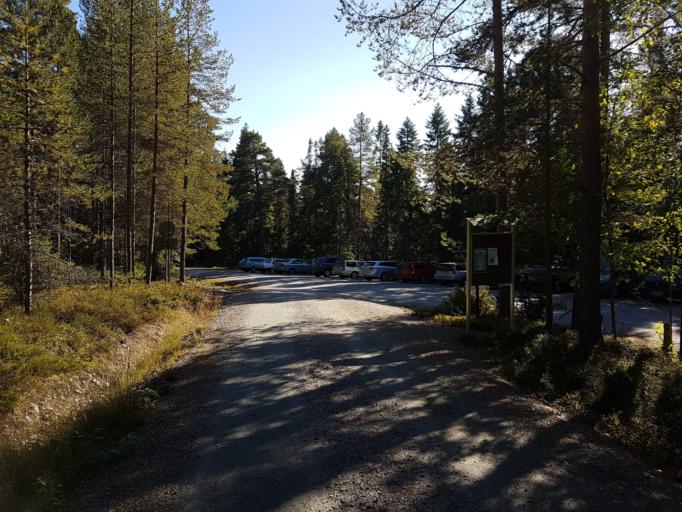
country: SE
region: Vaesterbotten
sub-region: Skelleftea Kommun
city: Skelleftehamn
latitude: 64.4759
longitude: 21.5759
